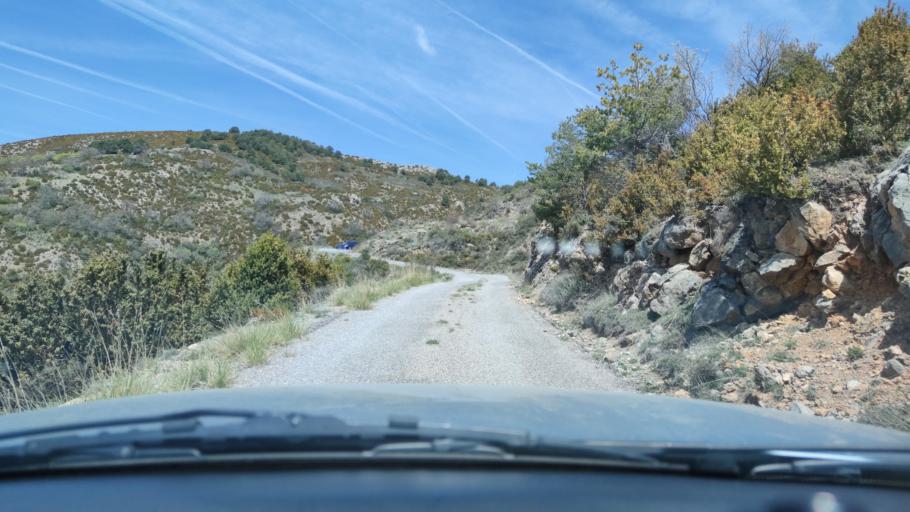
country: ES
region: Catalonia
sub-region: Provincia de Lleida
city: Sort
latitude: 42.2972
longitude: 1.1717
